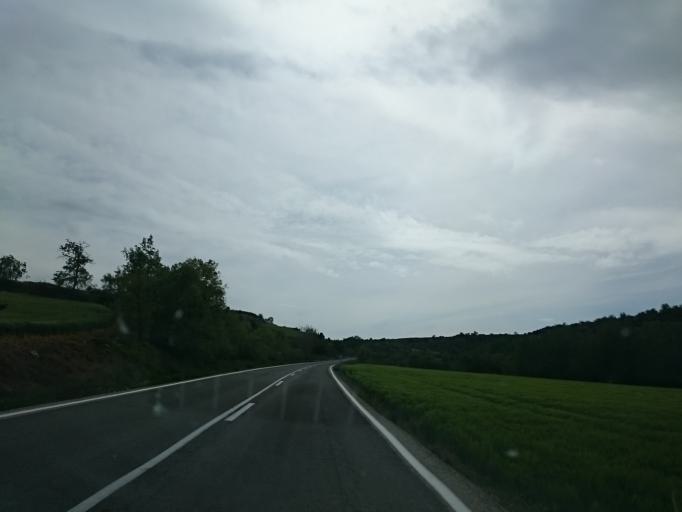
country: ES
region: Catalonia
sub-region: Provincia de Lleida
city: Tora de Riubregos
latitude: 41.7921
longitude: 1.3959
